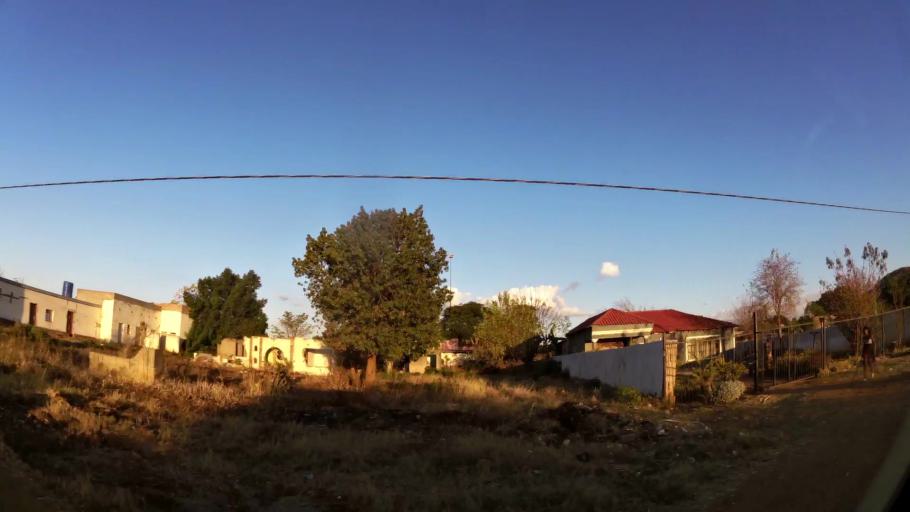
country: ZA
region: Limpopo
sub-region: Waterberg District Municipality
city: Mokopane
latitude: -24.1448
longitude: 28.9735
